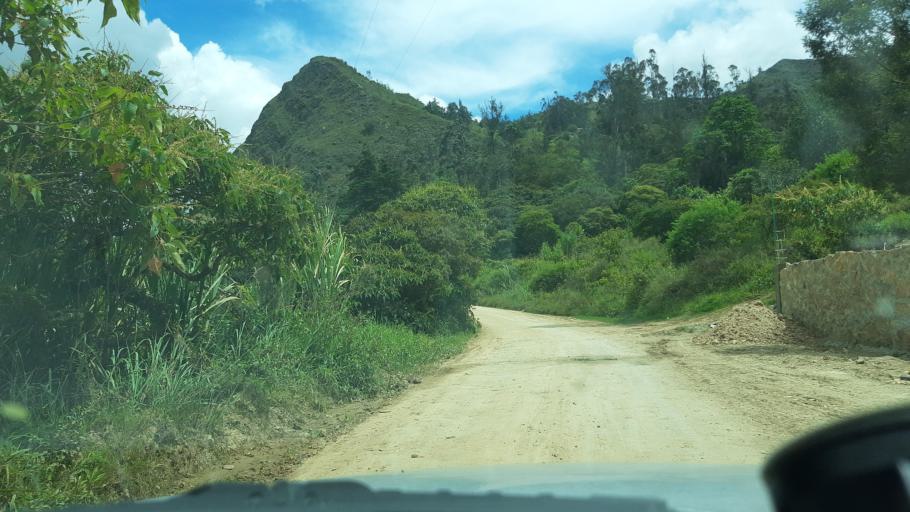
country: CO
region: Cundinamarca
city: Umbita
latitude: 5.2237
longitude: -73.4166
